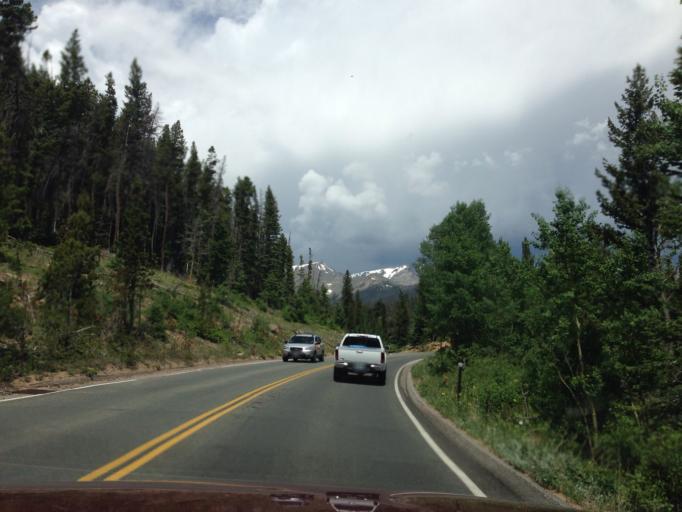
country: US
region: Colorado
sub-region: Larimer County
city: Estes Park
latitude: 40.3974
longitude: -105.6385
